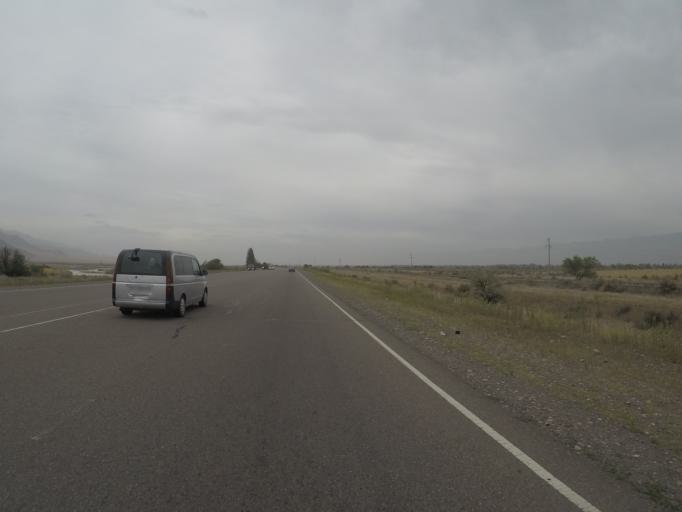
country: KG
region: Chuy
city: Tokmok
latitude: 42.8308
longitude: 75.4584
